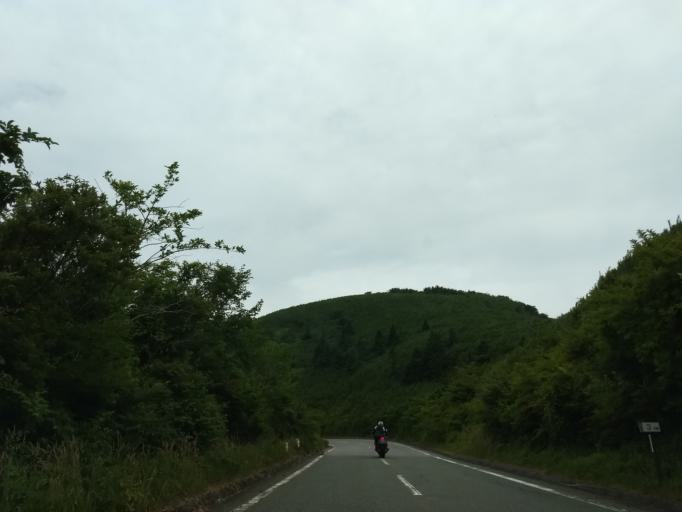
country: JP
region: Shizuoka
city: Gotemba
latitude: 35.2401
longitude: 138.9776
